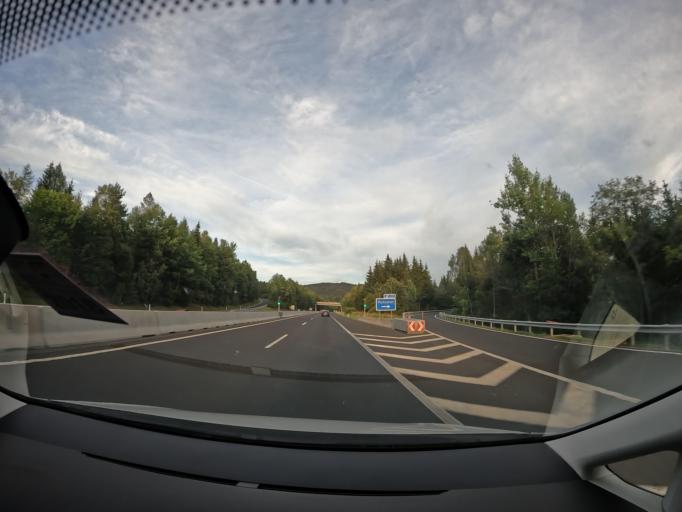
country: AT
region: Carinthia
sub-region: Politischer Bezirk Wolfsberg
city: Preitenegg
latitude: 46.9659
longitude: 14.9484
